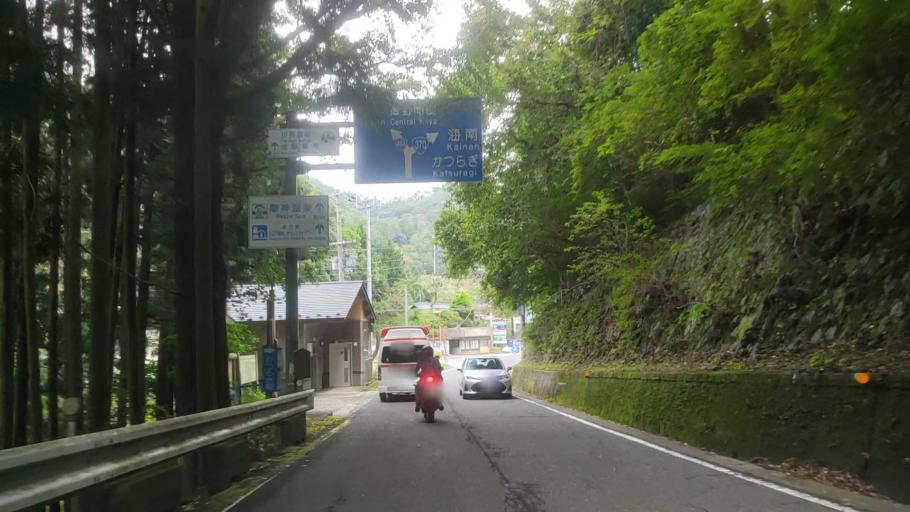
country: JP
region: Wakayama
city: Koya
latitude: 34.2204
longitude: 135.5373
